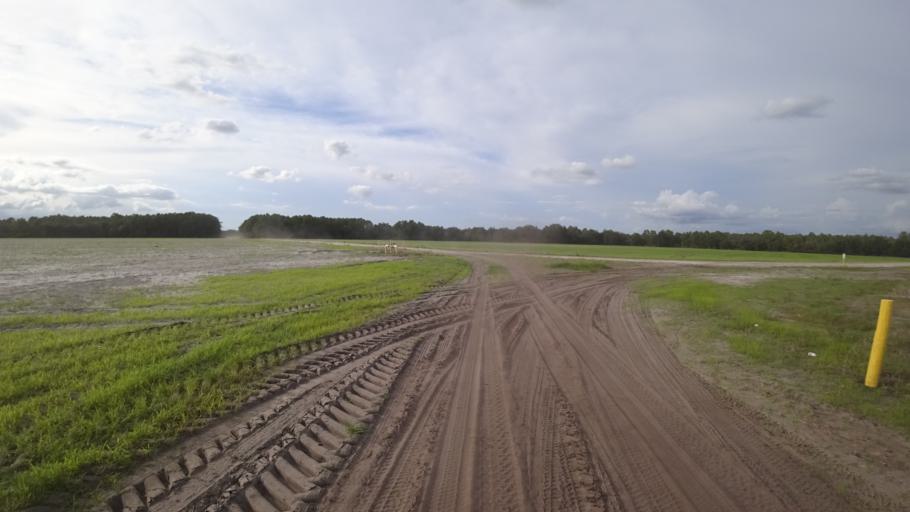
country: US
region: Florida
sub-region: Hillsborough County
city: Wimauma
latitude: 27.5613
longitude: -82.0958
